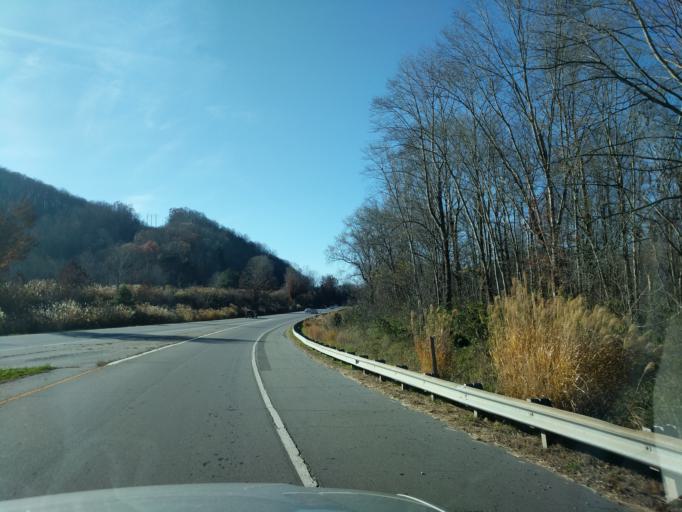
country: US
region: North Carolina
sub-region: Buncombe County
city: Swannanoa
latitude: 35.5951
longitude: -82.4044
